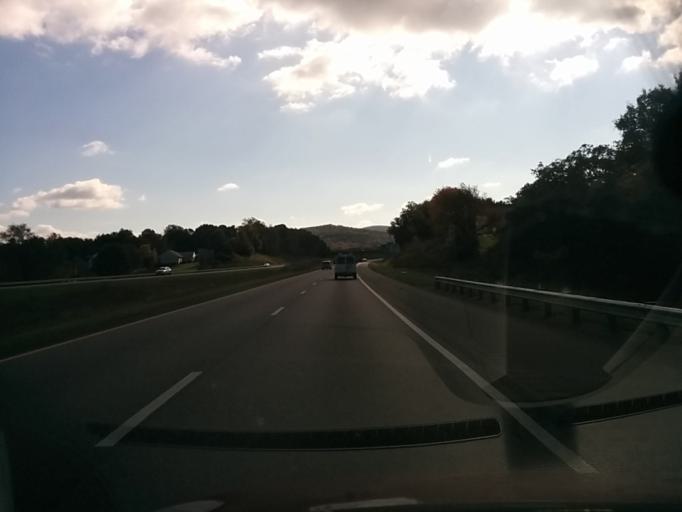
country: US
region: Virginia
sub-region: Augusta County
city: Lyndhurst
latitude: 38.0557
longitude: -78.9243
